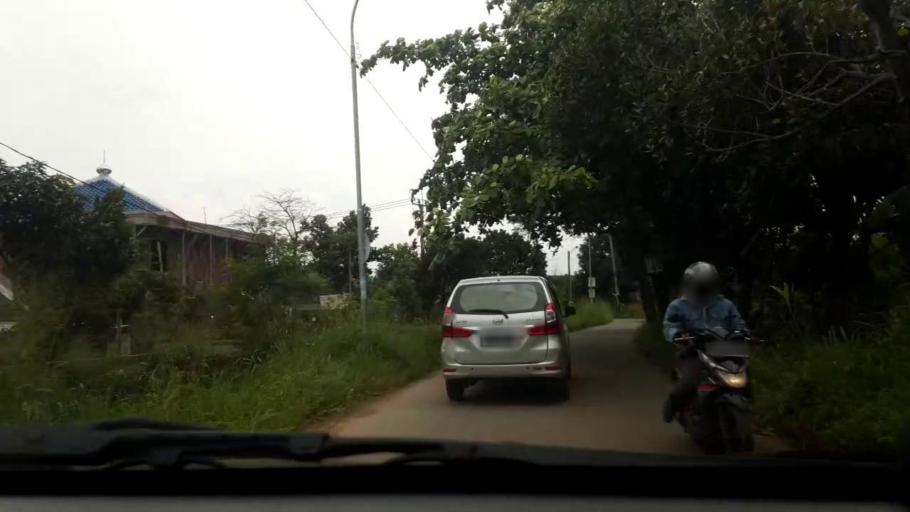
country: ID
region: West Java
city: Cileunyi
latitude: -6.9464
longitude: 107.7138
